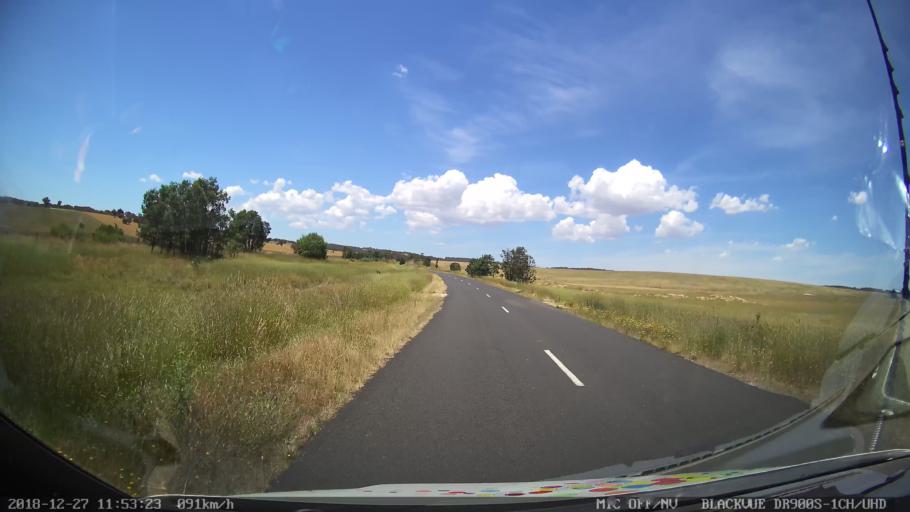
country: AU
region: New South Wales
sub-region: Blayney
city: Blayney
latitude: -33.6611
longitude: 149.4014
